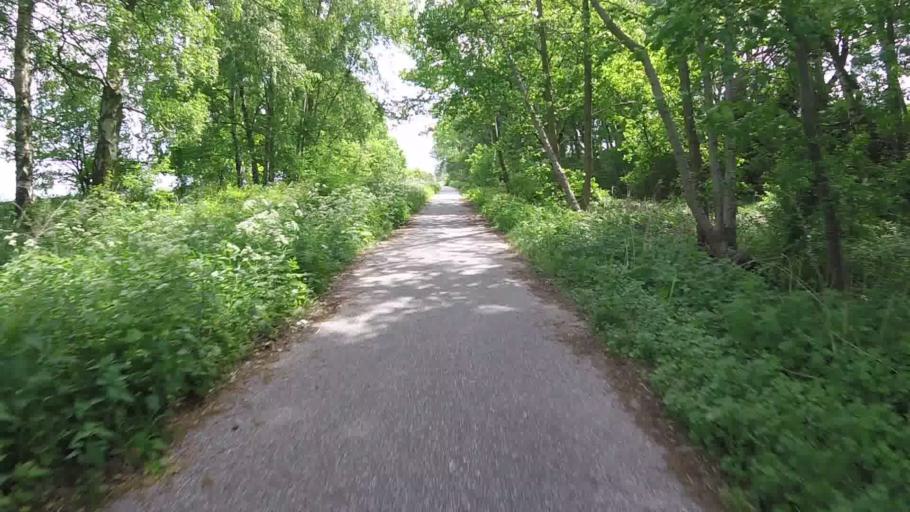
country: DE
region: Schleswig-Holstein
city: Oststeinbek
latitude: 53.4911
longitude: 10.1554
